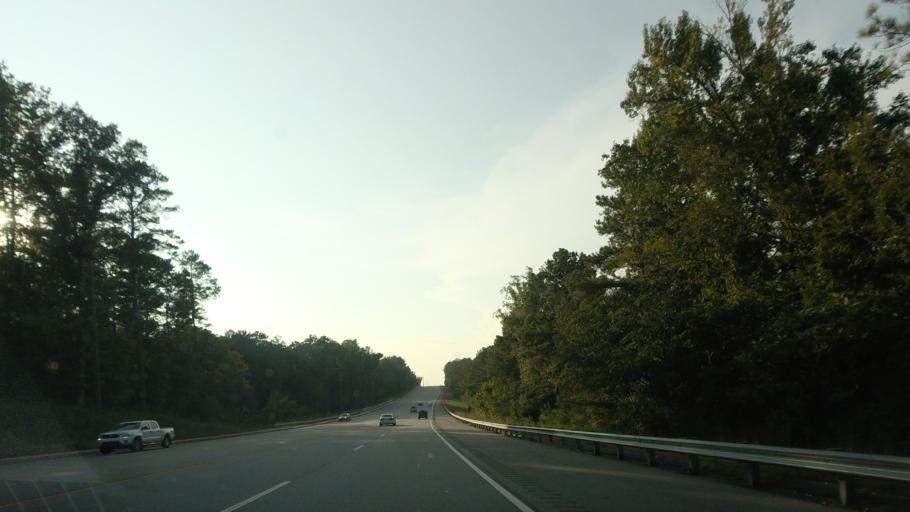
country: US
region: Georgia
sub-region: Bibb County
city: Macon
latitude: 32.9087
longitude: -83.6959
